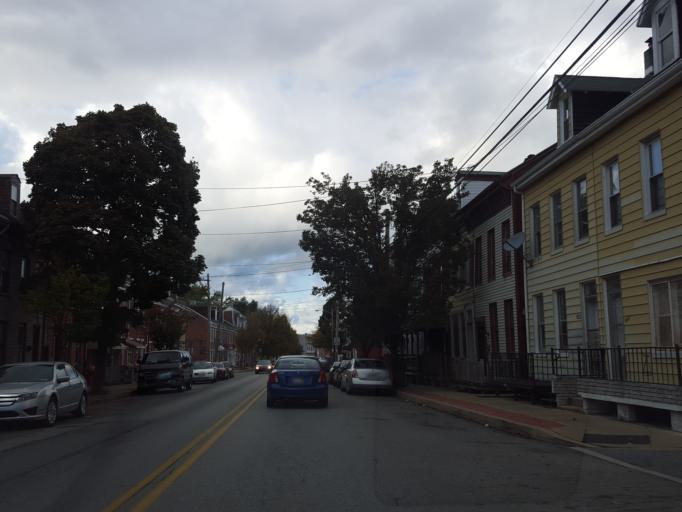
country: US
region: Pennsylvania
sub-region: York County
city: York
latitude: 39.9550
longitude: -76.7189
